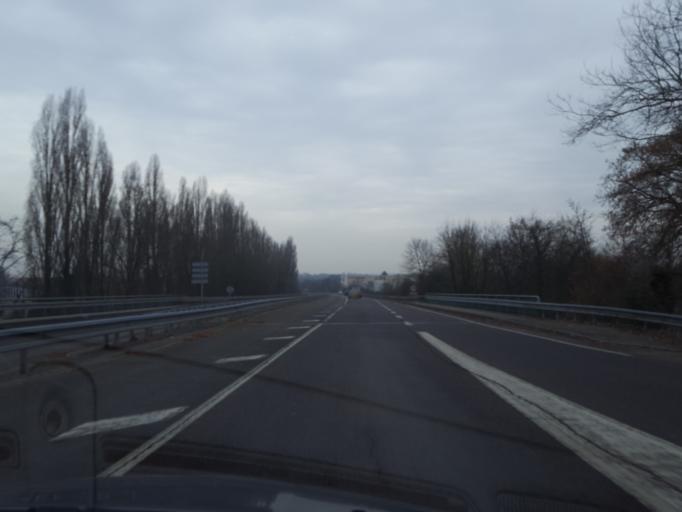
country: FR
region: Lorraine
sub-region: Departement de la Moselle
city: Moulins-les-Metz
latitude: 49.0948
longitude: 6.1195
